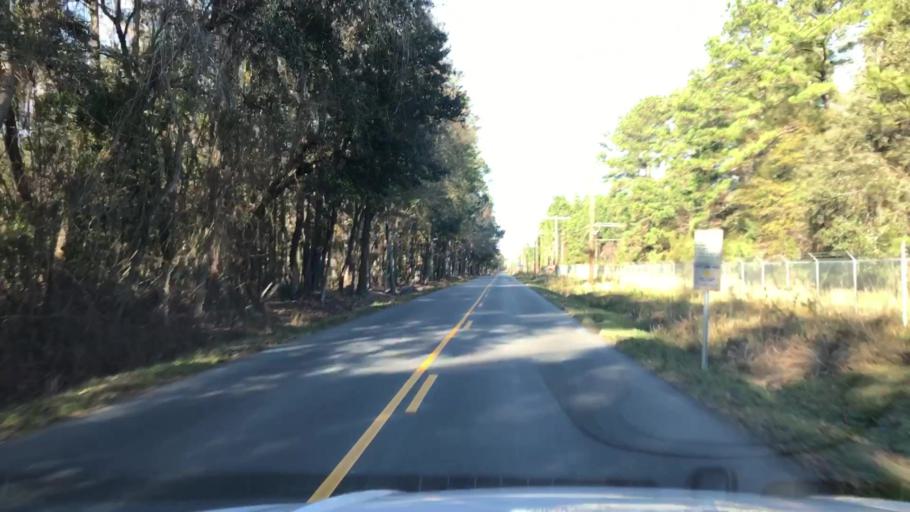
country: US
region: South Carolina
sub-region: Berkeley County
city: Ladson
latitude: 32.9869
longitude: -80.1120
